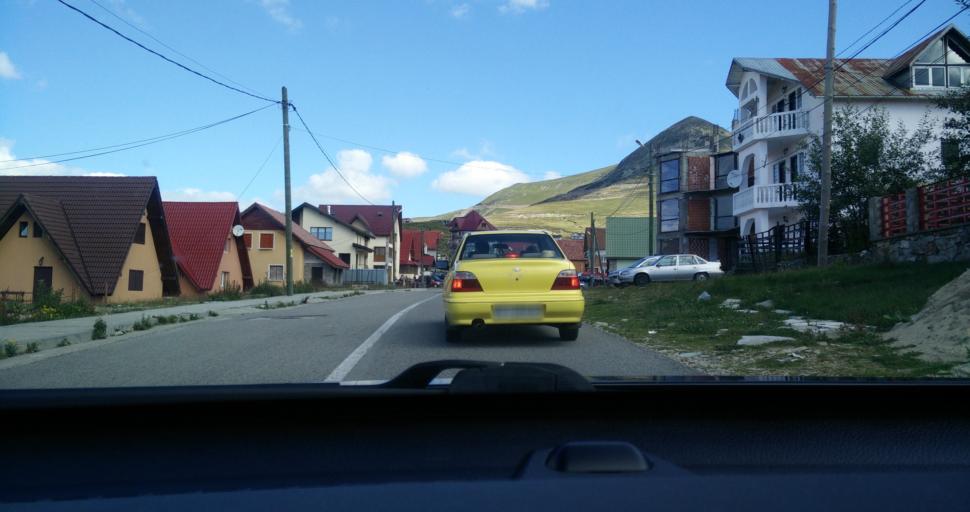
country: RO
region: Gorj
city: Novaci-Straini
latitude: 45.3065
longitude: 23.6846
